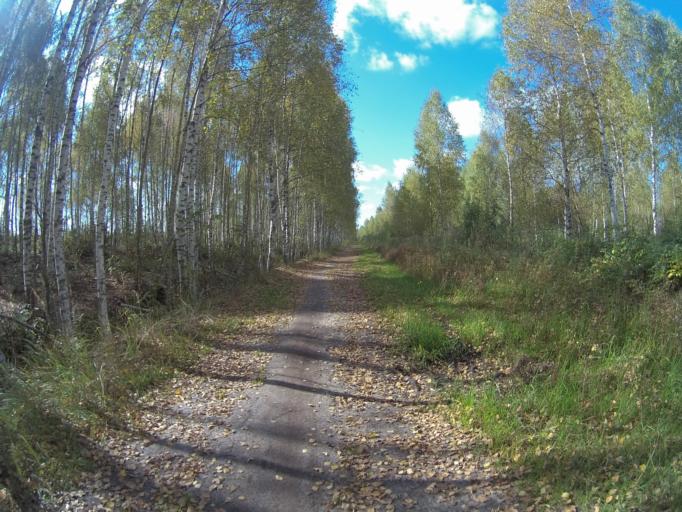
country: RU
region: Vladimir
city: Raduzhnyy
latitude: 55.9349
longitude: 40.2146
